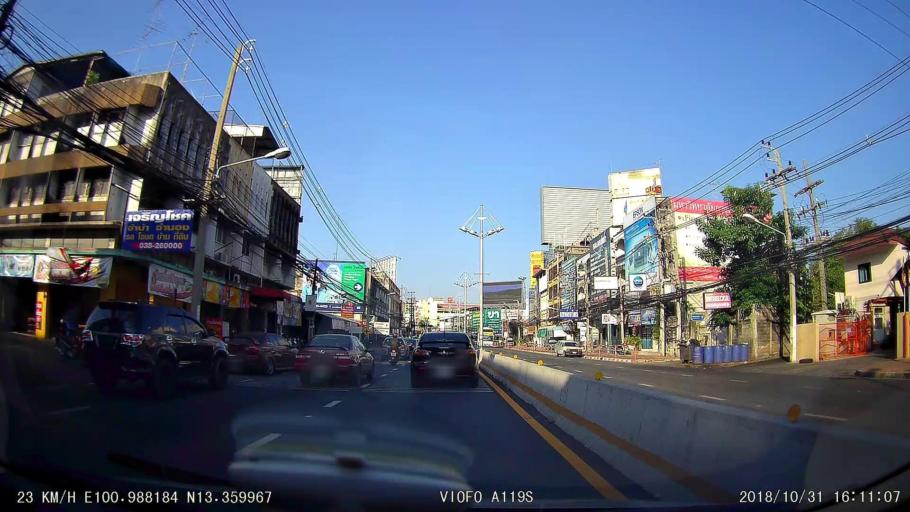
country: TH
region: Chon Buri
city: Chon Buri
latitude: 13.3602
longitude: 100.9883
